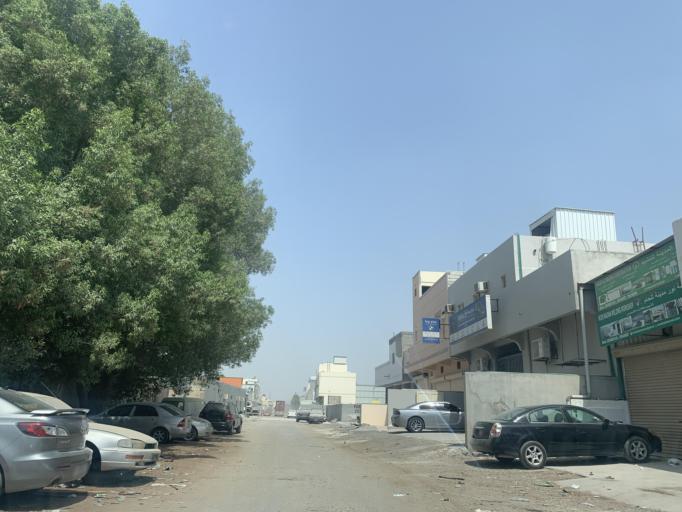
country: BH
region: Central Governorate
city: Madinat Hamad
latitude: 26.1406
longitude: 50.4826
